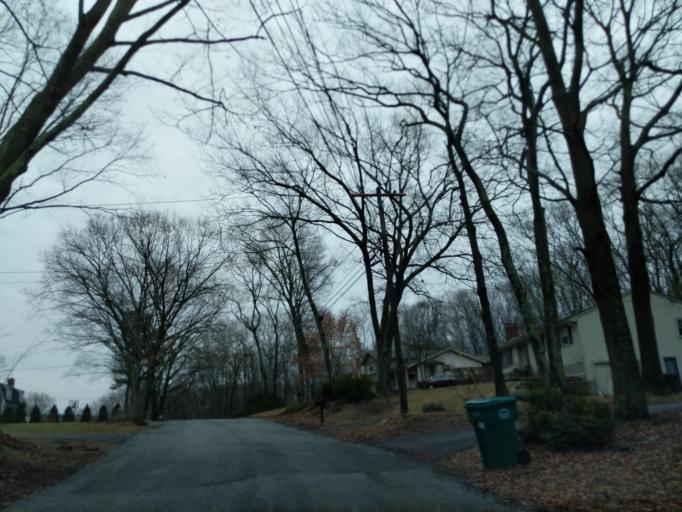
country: US
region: Massachusetts
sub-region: Worcester County
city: Whitinsville
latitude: 42.1070
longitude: -71.6929
